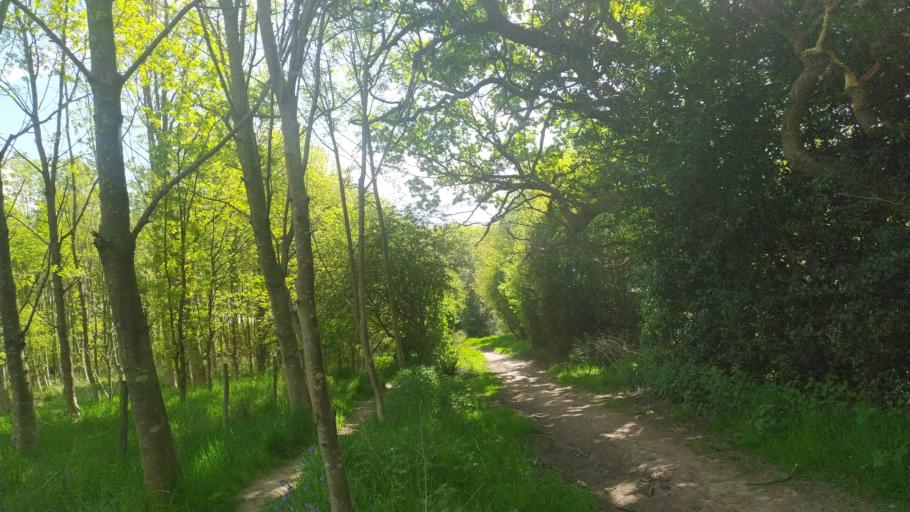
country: GB
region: England
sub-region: City and Borough of Leeds
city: Chapel Allerton
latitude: 53.8820
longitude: -1.5488
